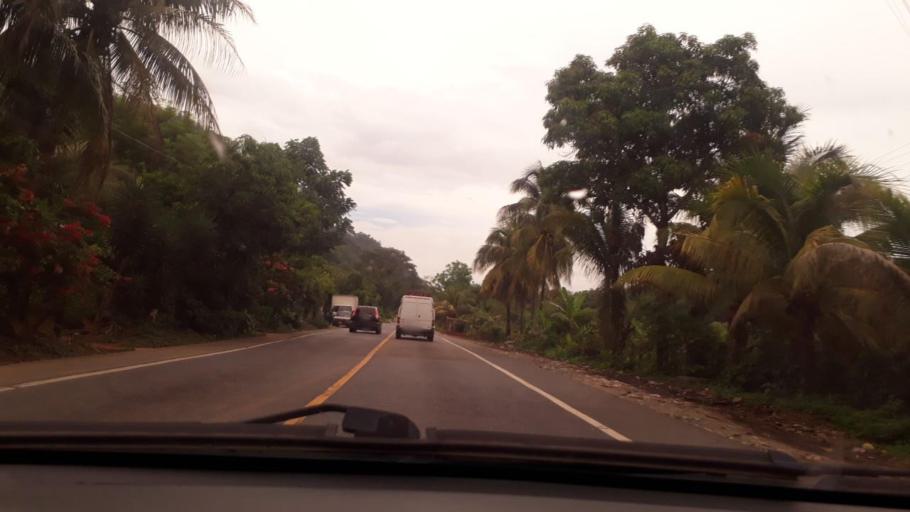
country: GT
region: Izabal
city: Morales
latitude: 15.5417
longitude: -88.7216
